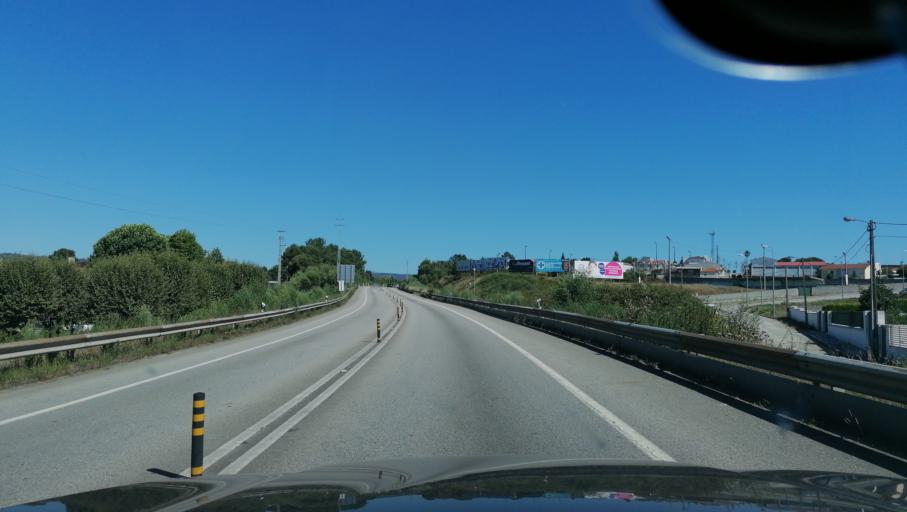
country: PT
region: Aveiro
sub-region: Santa Maria da Feira
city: Arrifana
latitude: 40.9205
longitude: -8.4990
